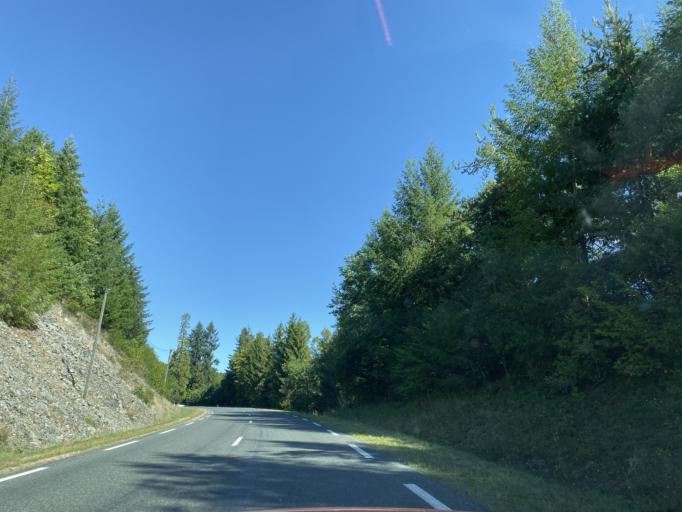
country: FR
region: Rhone-Alpes
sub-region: Departement de la Loire
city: Saint-Just-en-Chevalet
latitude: 45.8959
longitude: 3.8475
